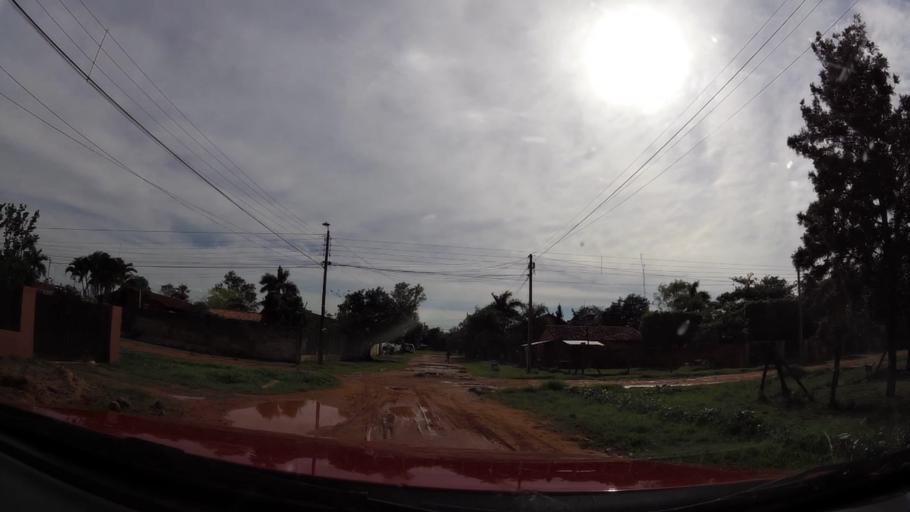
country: PY
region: Central
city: Limpio
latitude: -25.1786
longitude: -57.4933
